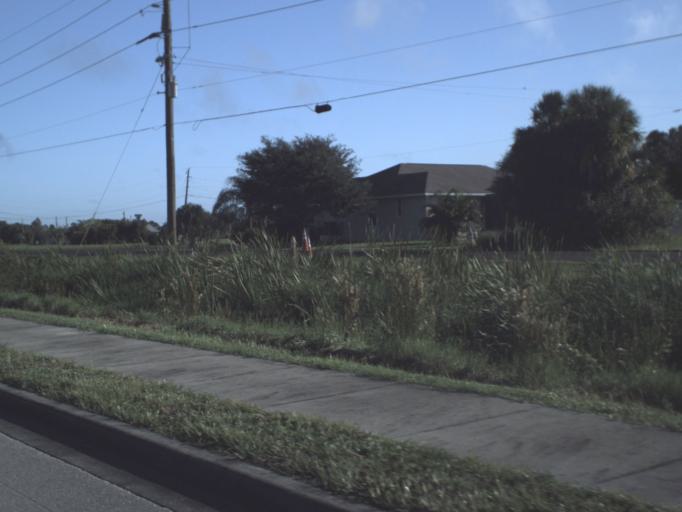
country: US
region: Florida
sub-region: Charlotte County
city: Cleveland
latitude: 26.9910
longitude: -81.9590
